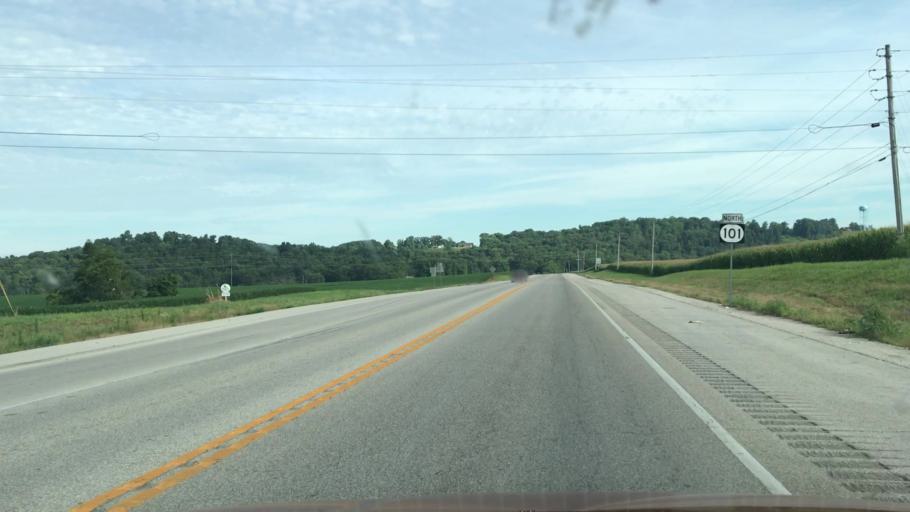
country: US
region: Kentucky
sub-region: Edmonson County
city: Brownsville
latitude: 37.0860
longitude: -86.2289
